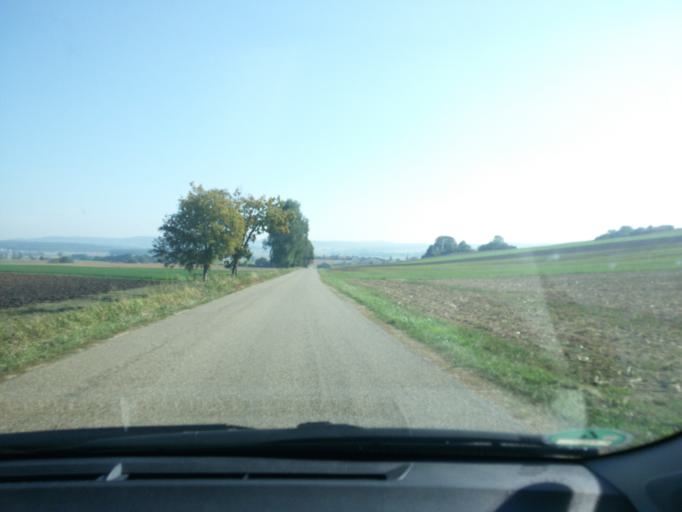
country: DE
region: Bavaria
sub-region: Swabia
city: Hainsfarth
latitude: 48.9818
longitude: 10.5927
